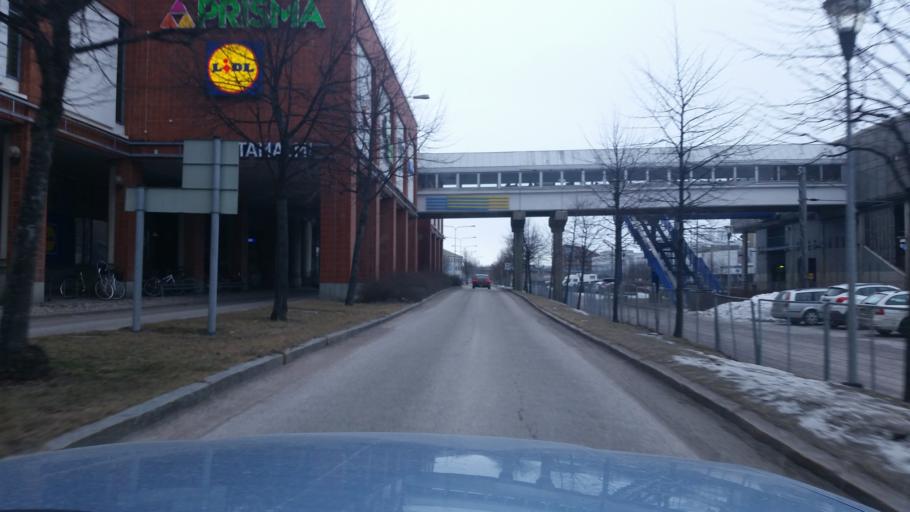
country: FI
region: Uusimaa
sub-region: Helsinki
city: Vantaa
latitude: 60.2512
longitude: 25.0102
